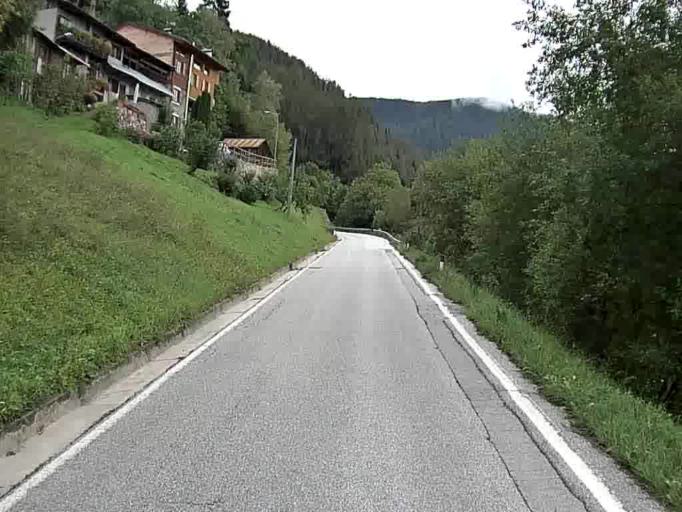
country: IT
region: Trentino-Alto Adige
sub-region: Provincia di Trento
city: Frassilongo
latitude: 46.0827
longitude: 11.2913
